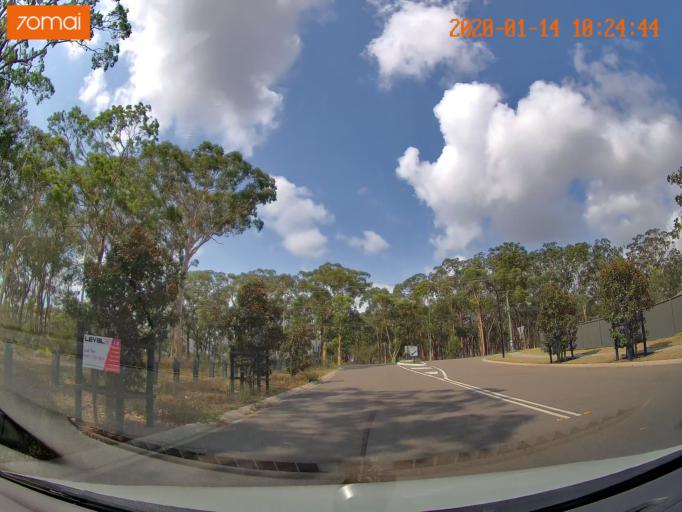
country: AU
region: New South Wales
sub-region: Lake Macquarie Shire
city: Dora Creek
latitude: -33.1119
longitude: 151.5111
